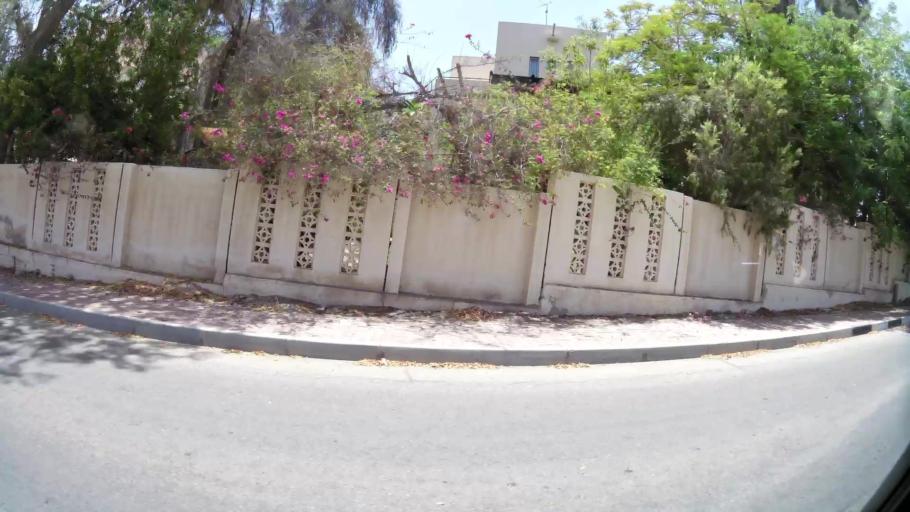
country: OM
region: Muhafazat Masqat
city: Bawshar
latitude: 23.6084
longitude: 58.4655
